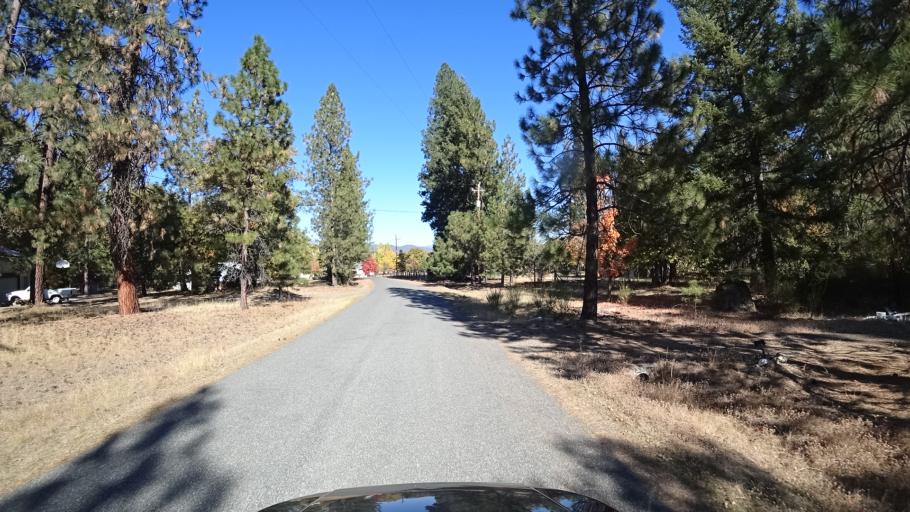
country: US
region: California
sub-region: Siskiyou County
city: Yreka
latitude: 41.5205
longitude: -122.9230
